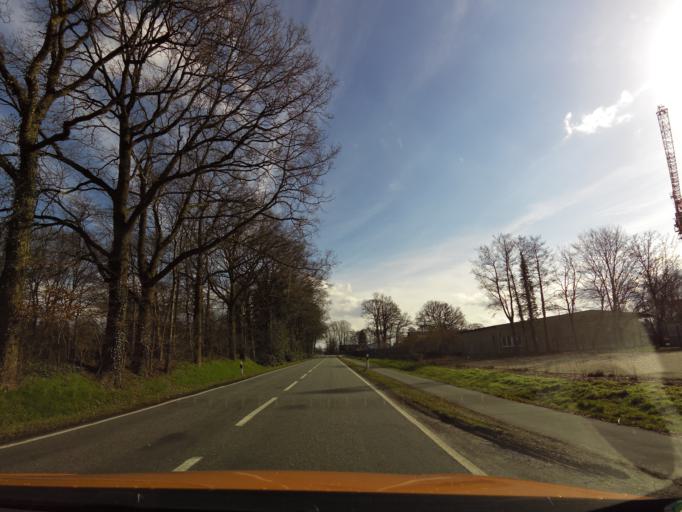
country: DE
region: Lower Saxony
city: Hatten
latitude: 53.0797
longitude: 8.2950
